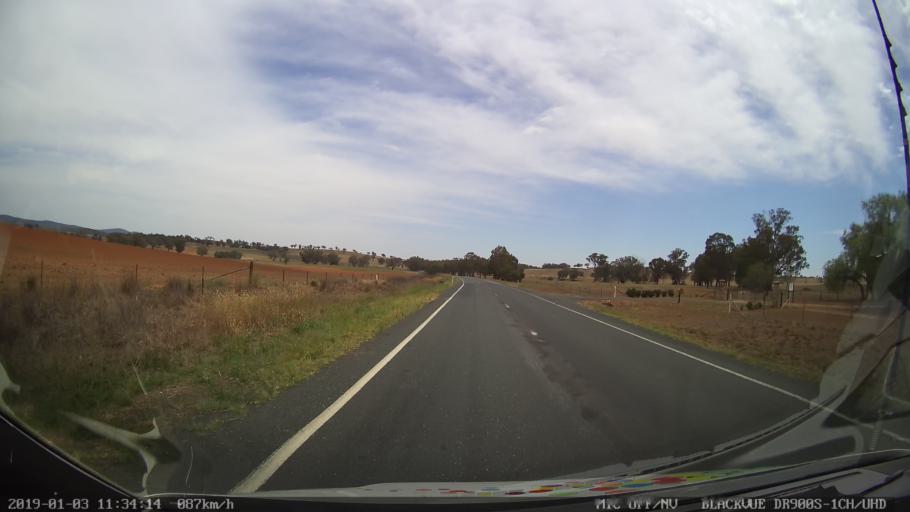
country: AU
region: New South Wales
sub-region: Weddin
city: Grenfell
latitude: -33.9373
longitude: 148.1654
